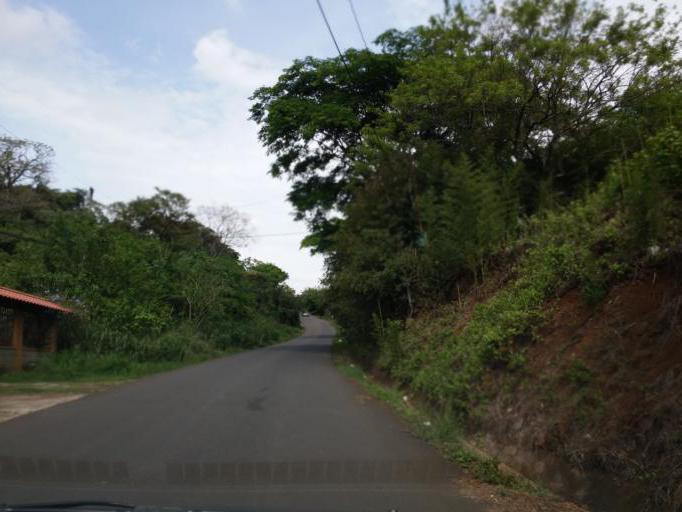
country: CR
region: Alajuela
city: Alajuela
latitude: 10.0088
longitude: -84.1995
